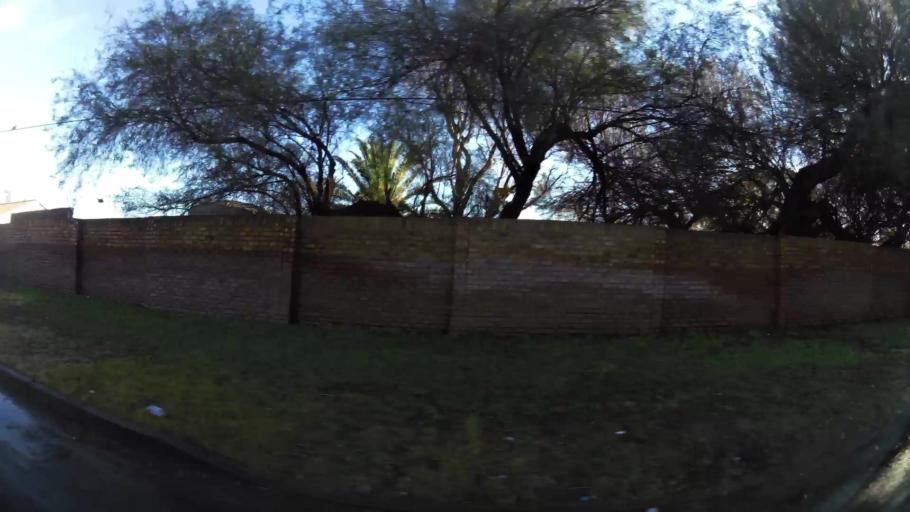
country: ZA
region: Northern Cape
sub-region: Frances Baard District Municipality
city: Kimberley
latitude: -28.7487
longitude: 24.7357
